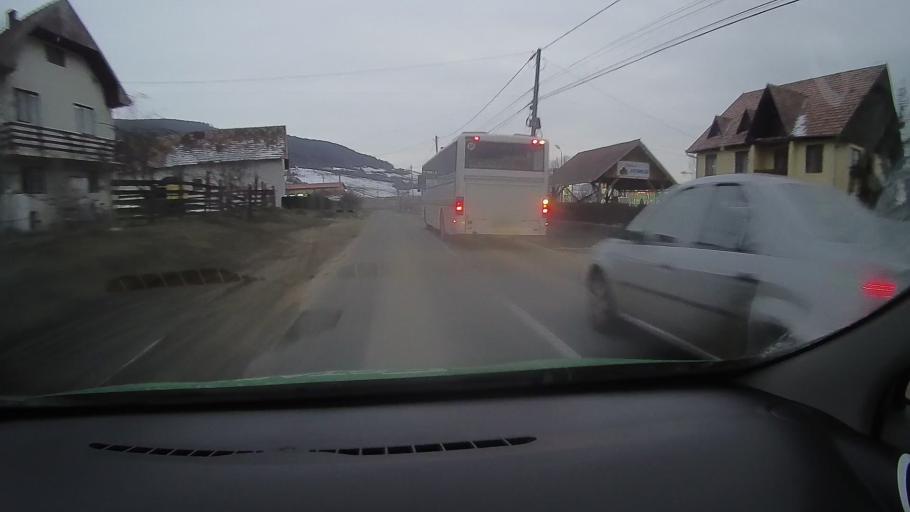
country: RO
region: Harghita
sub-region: Municipiul Odorheiu Secuiesc
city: Odorheiu Secuiesc
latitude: 46.2845
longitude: 25.2897
